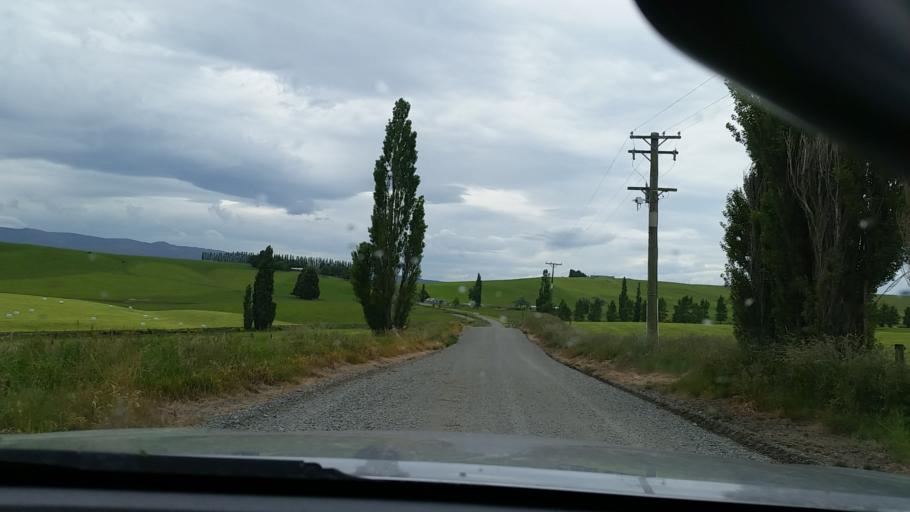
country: NZ
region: Southland
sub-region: Southland District
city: Winton
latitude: -45.8921
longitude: 168.1414
